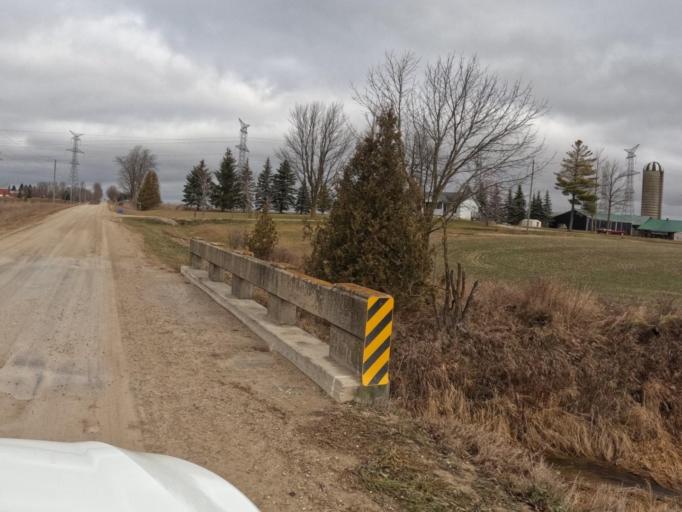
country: CA
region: Ontario
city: Shelburne
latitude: 43.9910
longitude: -80.4074
